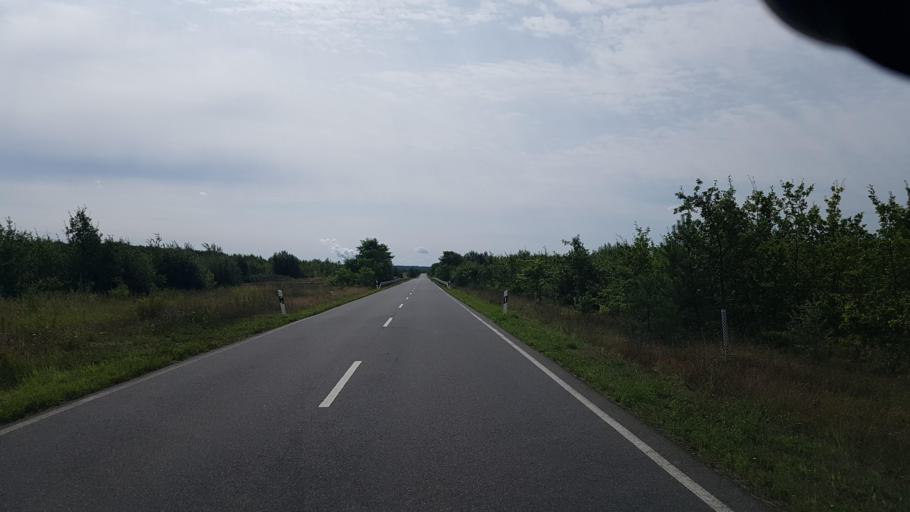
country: DE
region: Brandenburg
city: Drebkau
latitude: 51.6044
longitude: 14.2761
